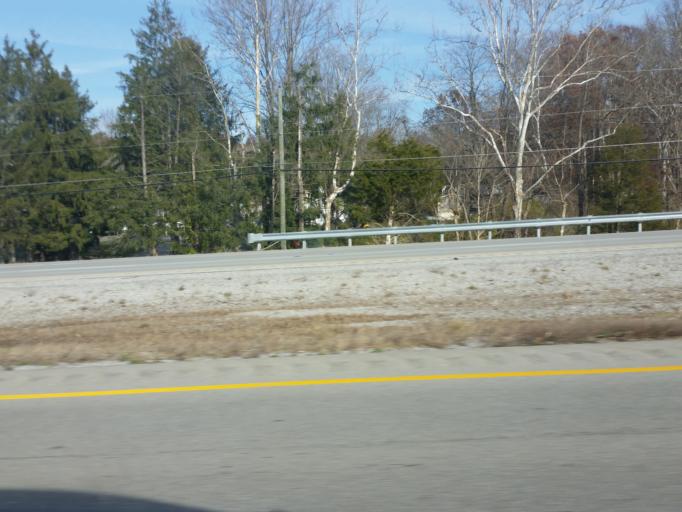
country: US
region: Kentucky
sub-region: Campbell County
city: Claryville
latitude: 38.8592
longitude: -84.3889
